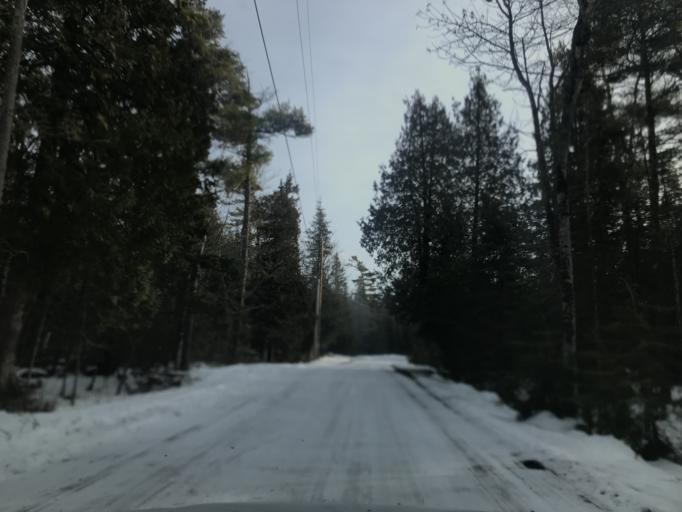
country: US
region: Wisconsin
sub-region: Door County
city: Sturgeon Bay
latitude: 45.1427
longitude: -87.0523
